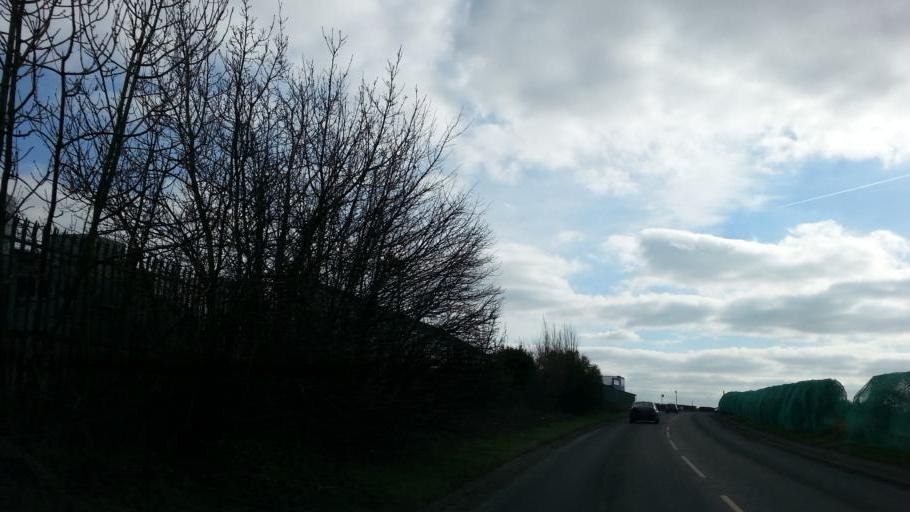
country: GB
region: England
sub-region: Staffordshire
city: Lichfield
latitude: 52.6680
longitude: -1.8316
